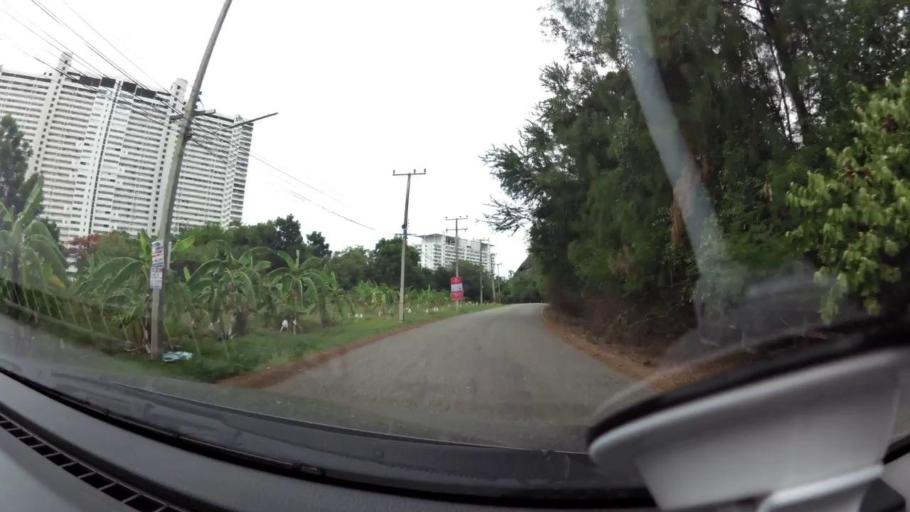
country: TH
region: Prachuap Khiri Khan
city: Pran Buri
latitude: 12.4335
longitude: 99.9773
